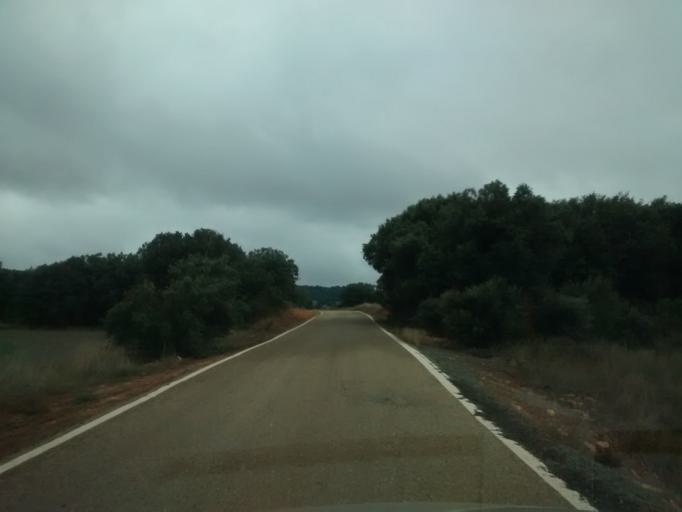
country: ES
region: Aragon
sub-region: Provincia de Zaragoza
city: Gallocanta
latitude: 40.9901
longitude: -1.4740
